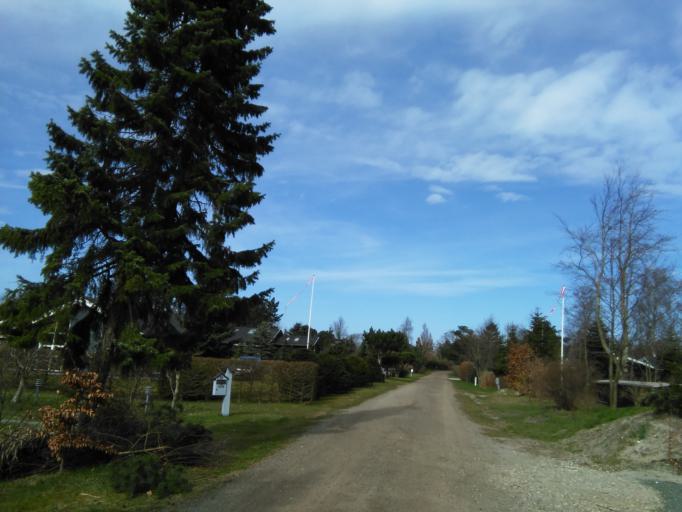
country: DK
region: Central Jutland
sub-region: Arhus Kommune
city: Malling
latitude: 55.9689
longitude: 10.2544
